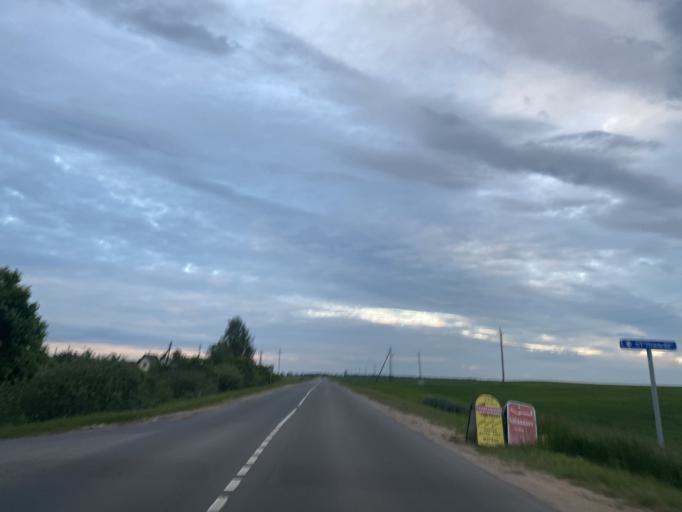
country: BY
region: Minsk
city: Rudzyensk
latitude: 53.6103
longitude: 27.8045
